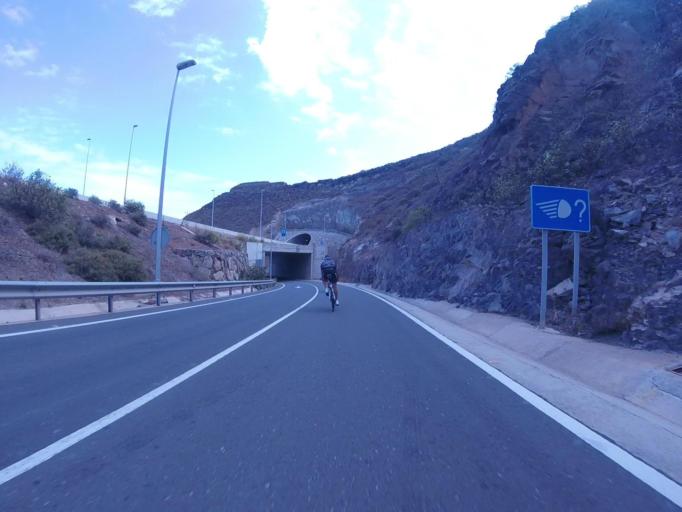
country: ES
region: Canary Islands
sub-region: Provincia de Las Palmas
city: Guia
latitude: 28.1397
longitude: -15.5947
